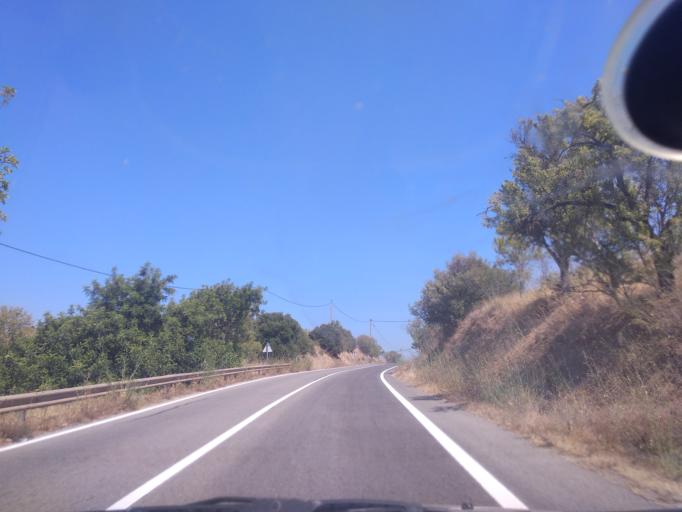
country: PT
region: Faro
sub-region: Lagos
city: Lagos
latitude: 37.1174
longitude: -8.6901
